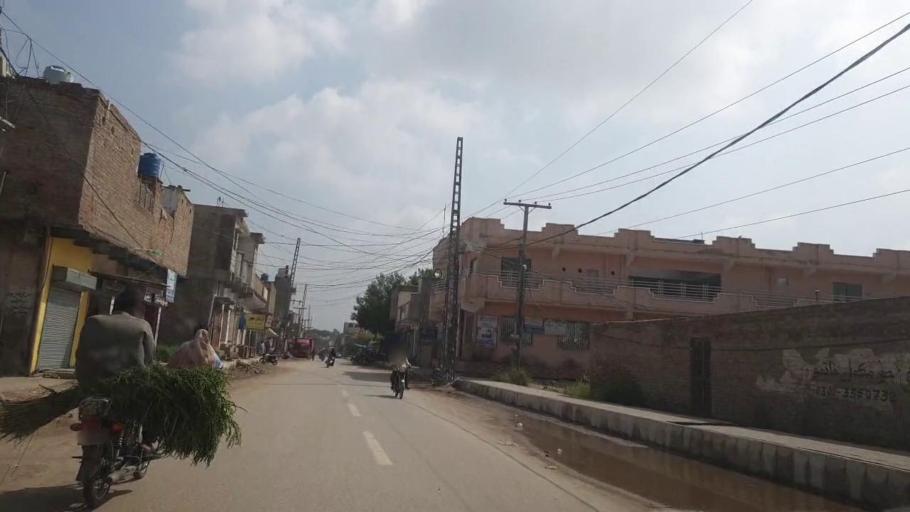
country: PK
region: Sindh
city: Khairpur
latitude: 27.5314
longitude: 68.7485
